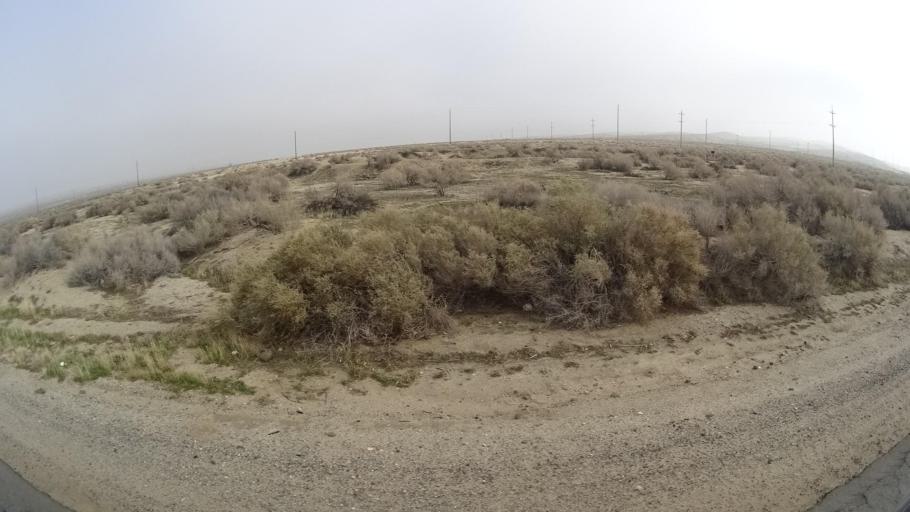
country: US
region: California
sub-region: Kern County
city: Ford City
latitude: 35.1814
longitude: -119.4291
